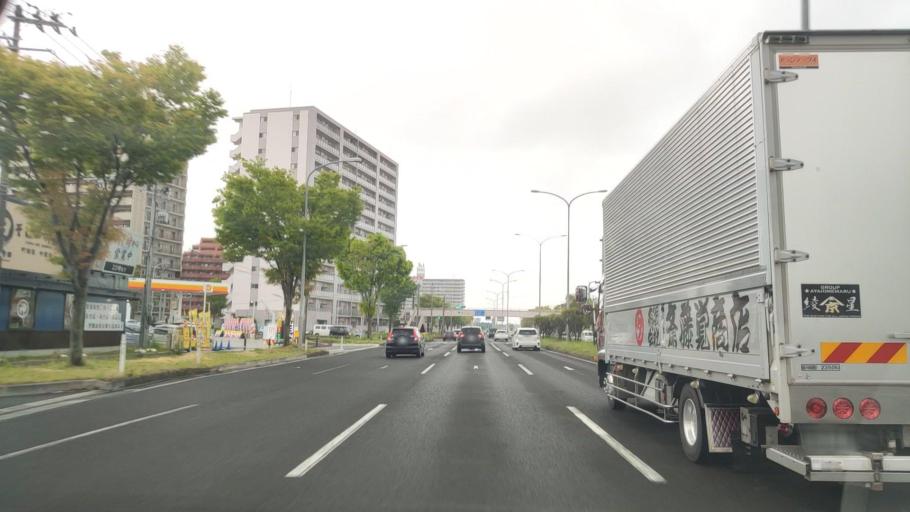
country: JP
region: Miyagi
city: Sendai-shi
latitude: 38.2453
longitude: 140.9233
